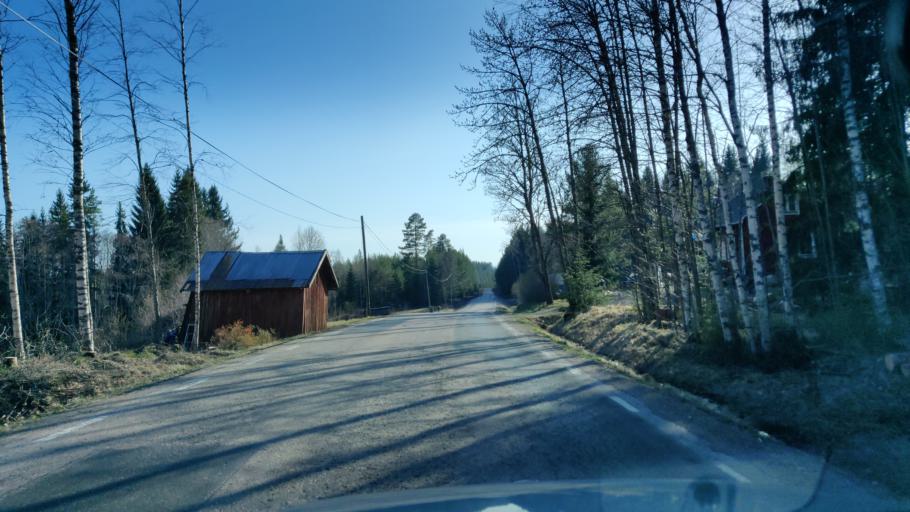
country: SE
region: Vaermland
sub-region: Sunne Kommun
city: Sunne
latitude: 59.9846
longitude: 13.2644
